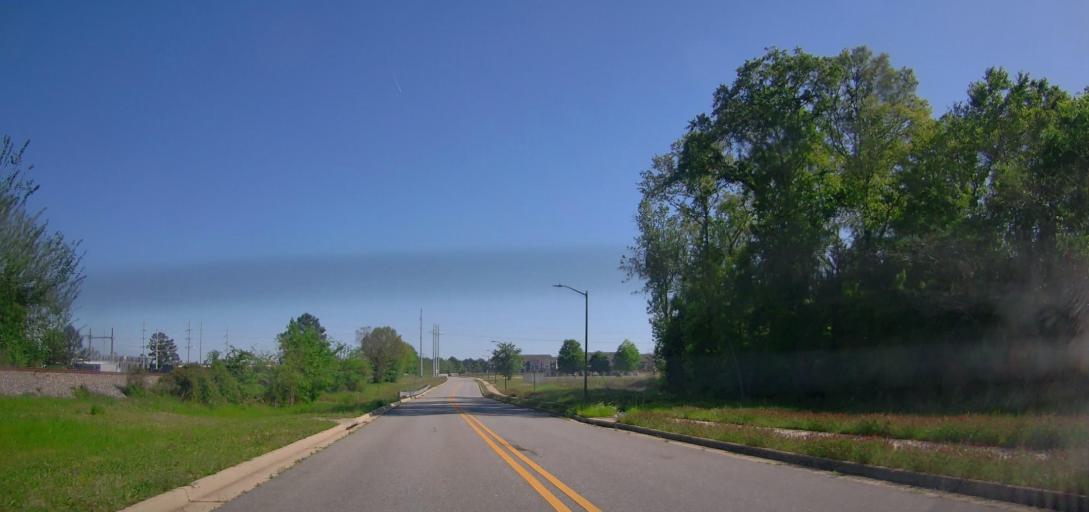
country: US
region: Georgia
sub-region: Houston County
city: Robins Air Force Base
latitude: 32.6079
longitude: -83.5962
